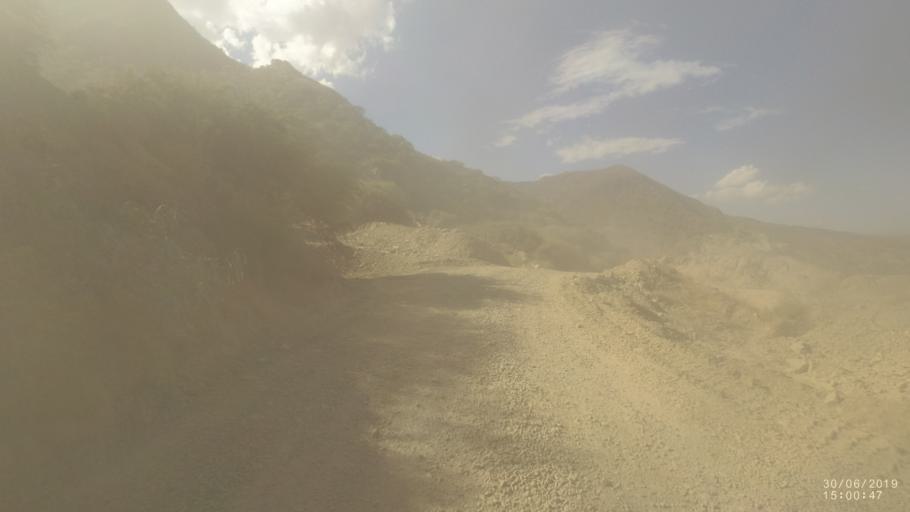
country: BO
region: Cochabamba
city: Irpa Irpa
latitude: -17.7353
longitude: -66.3395
